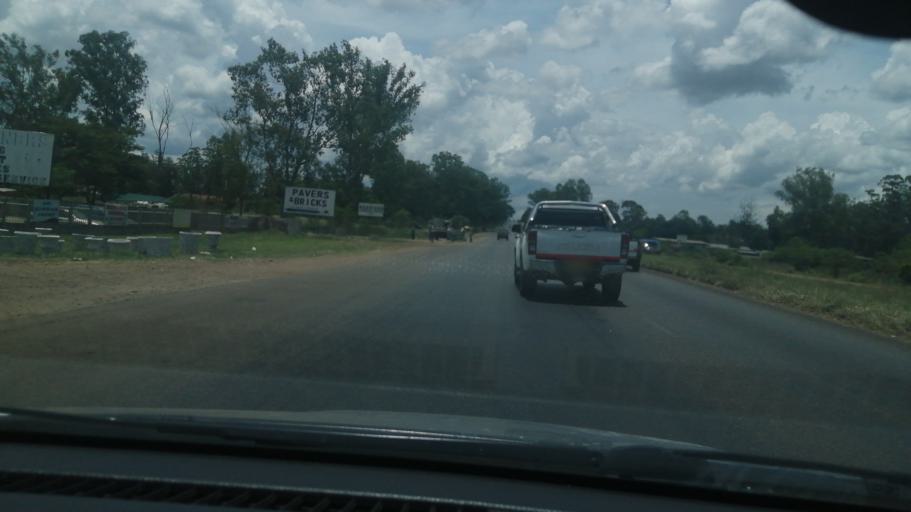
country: ZW
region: Harare
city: Harare
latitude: -17.8216
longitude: 30.9567
